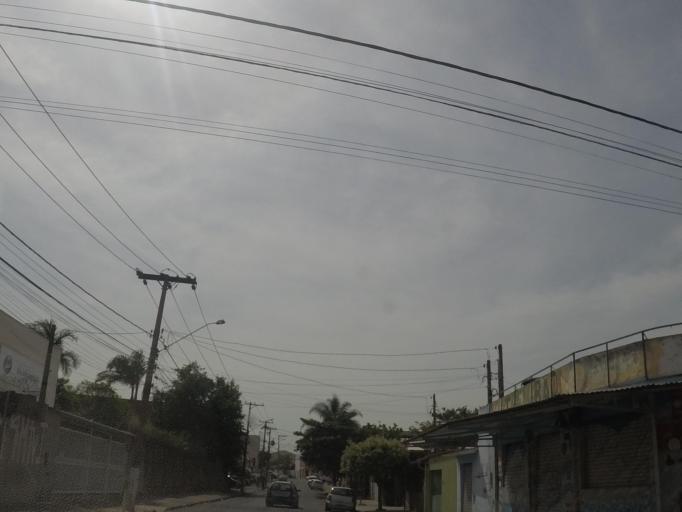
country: BR
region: Sao Paulo
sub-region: Hortolandia
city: Hortolandia
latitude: -22.8505
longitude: -47.1934
